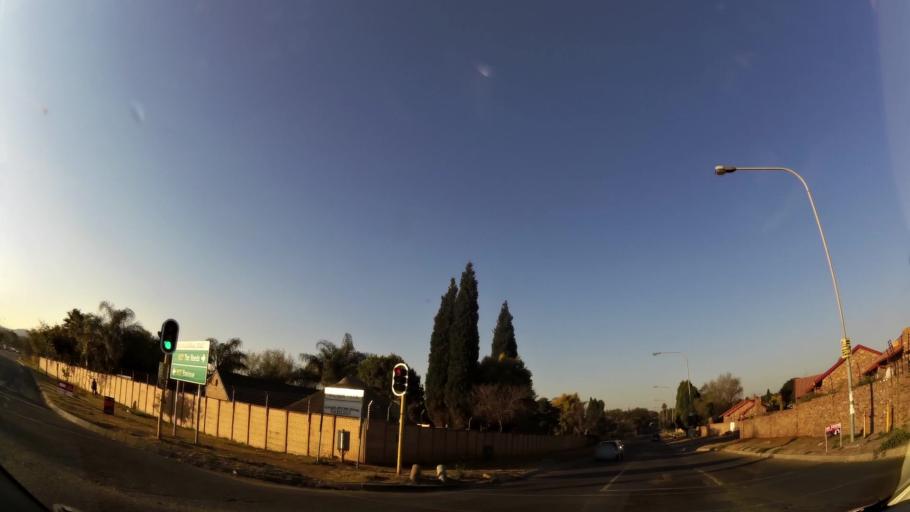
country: ZA
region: Gauteng
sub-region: City of Tshwane Metropolitan Municipality
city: Centurion
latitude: -25.8732
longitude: 28.1394
